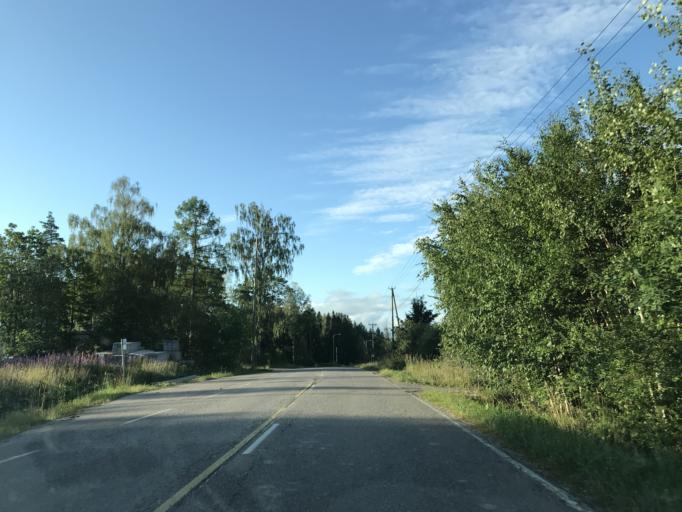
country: FI
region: Uusimaa
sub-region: Helsinki
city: Nurmijaervi
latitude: 60.3681
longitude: 24.6819
